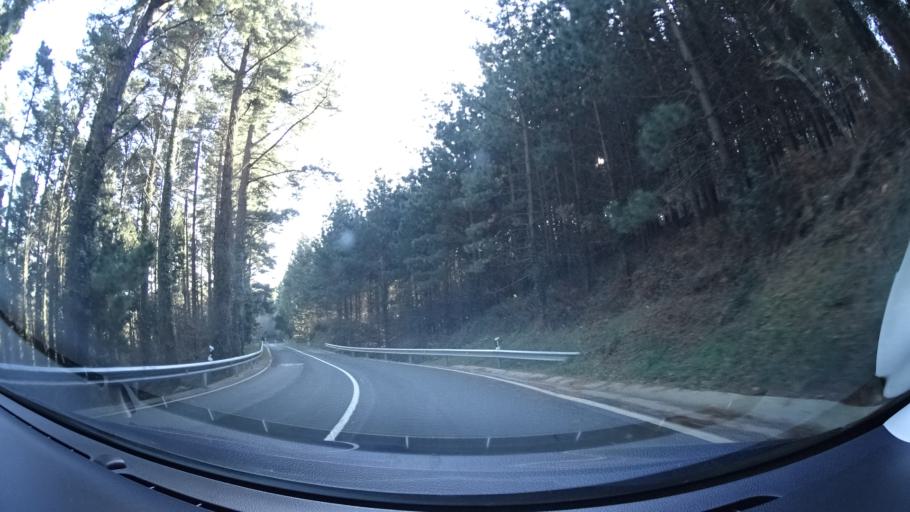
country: ES
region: Basque Country
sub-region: Bizkaia
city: Bermeo
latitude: 43.4374
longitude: -2.7487
